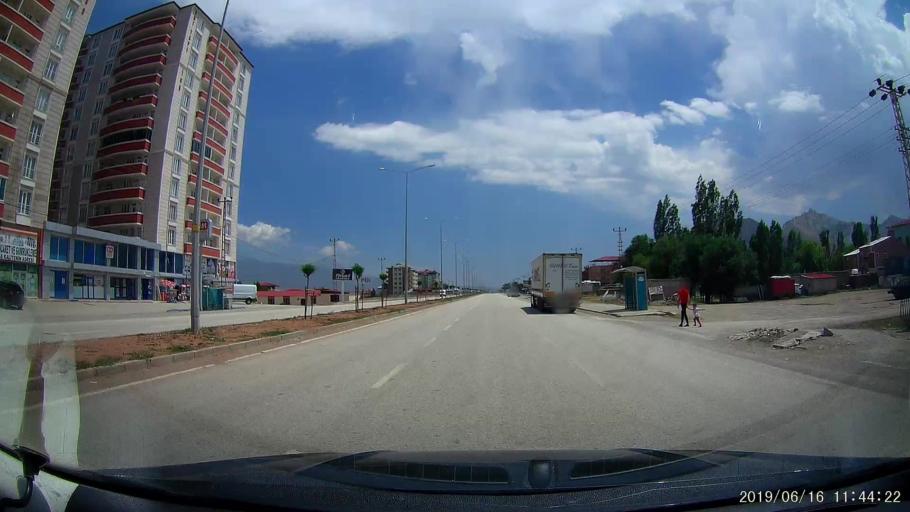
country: TR
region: Agri
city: Dogubayazit
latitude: 39.5572
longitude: 44.0881
